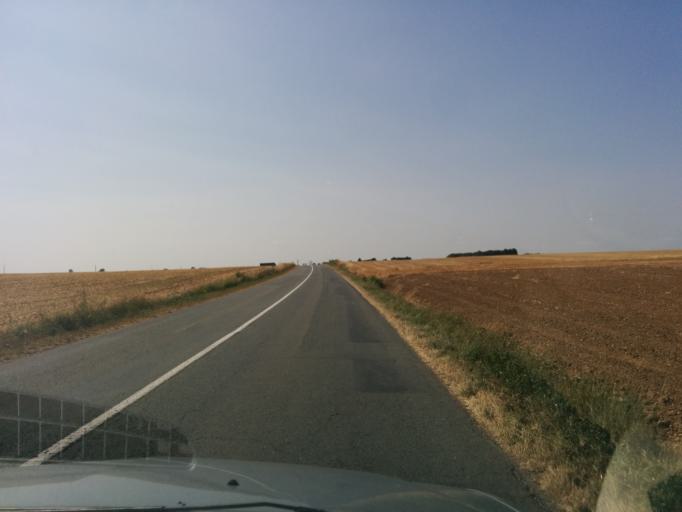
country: FR
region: Poitou-Charentes
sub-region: Departement de la Vienne
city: Mirebeau
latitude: 46.7816
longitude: 0.1321
